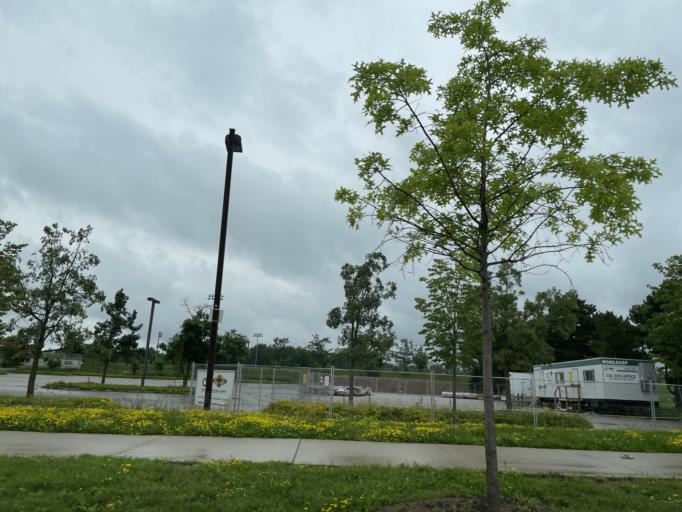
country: CA
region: Ontario
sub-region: Wellington County
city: Guelph
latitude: 43.5328
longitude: -80.2215
